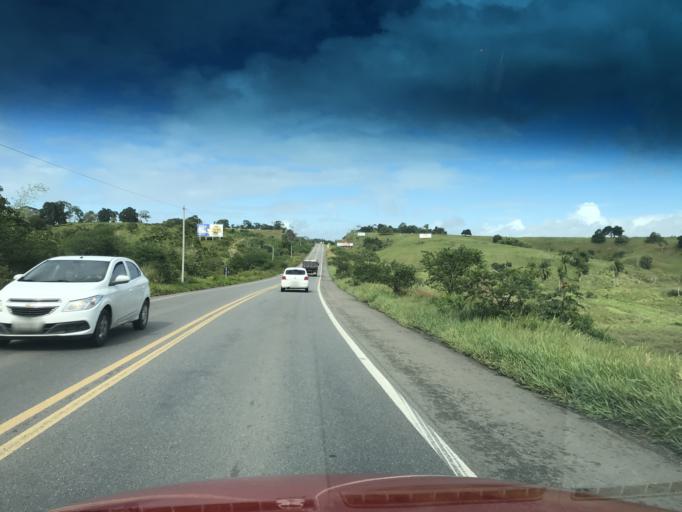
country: BR
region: Bahia
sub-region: Conceicao Do Almeida
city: Muritiba
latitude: -12.9066
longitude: -39.2385
